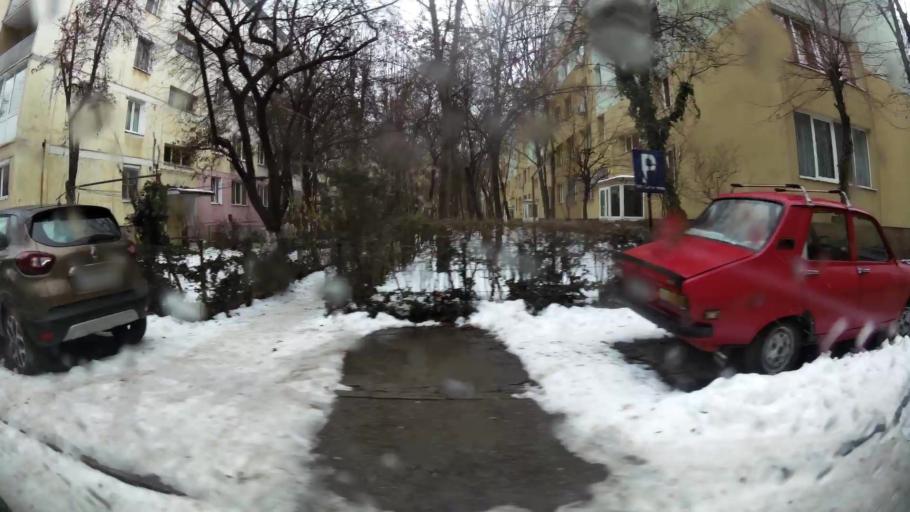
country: RO
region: Ilfov
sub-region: Comuna Chiajna
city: Rosu
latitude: 44.4143
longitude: 26.0194
